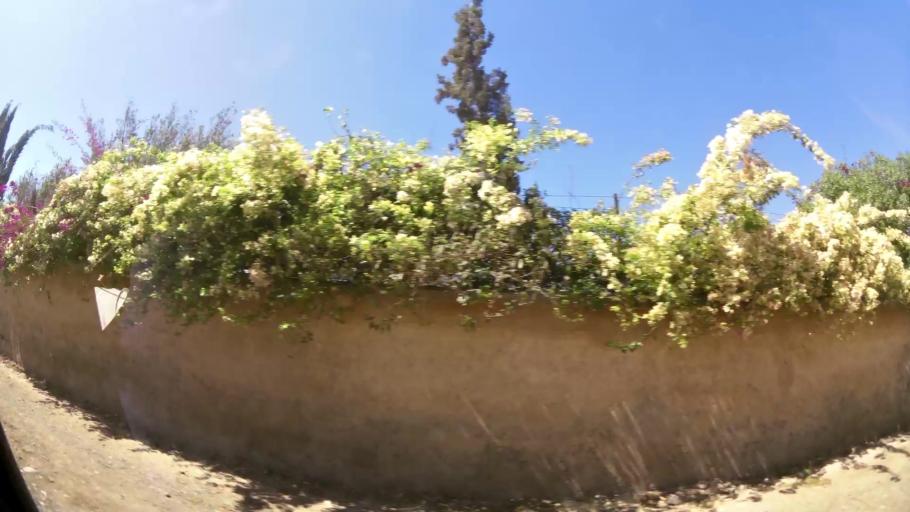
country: MA
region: Marrakech-Tensift-Al Haouz
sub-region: Marrakech
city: Marrakesh
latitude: 31.6732
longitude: -7.9847
